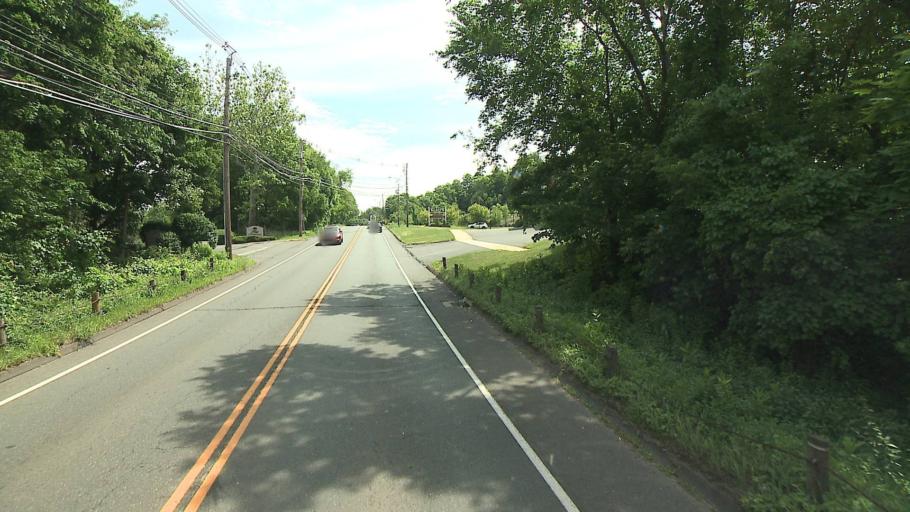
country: US
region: Connecticut
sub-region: Fairfield County
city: Danbury
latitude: 41.4001
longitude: -73.4285
